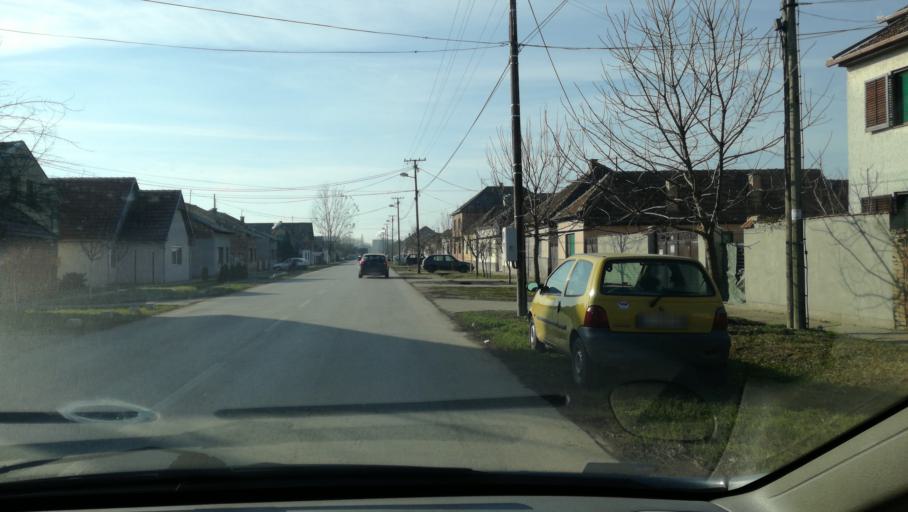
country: RS
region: Autonomna Pokrajina Vojvodina
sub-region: Severnobanatski Okrug
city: Kikinda
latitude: 45.8164
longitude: 20.4628
